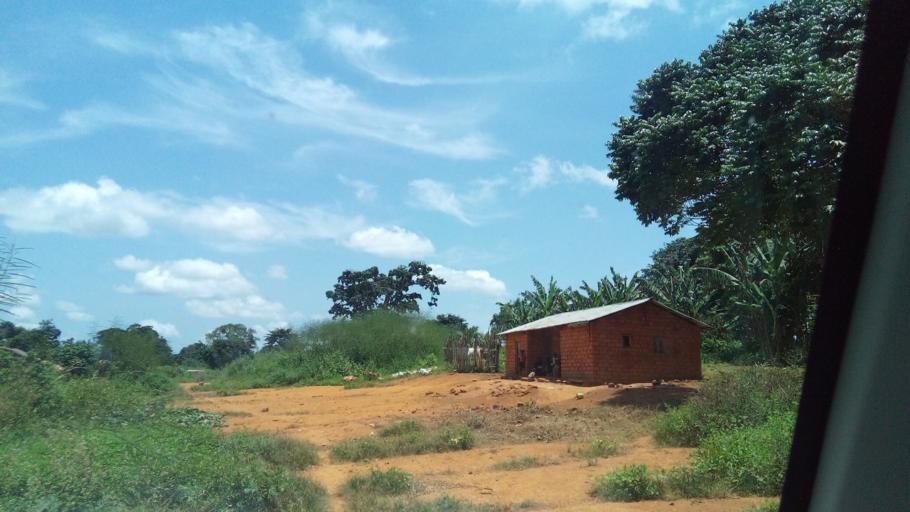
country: AO
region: Zaire
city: Mbanza Congo
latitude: -5.8063
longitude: 14.2385
